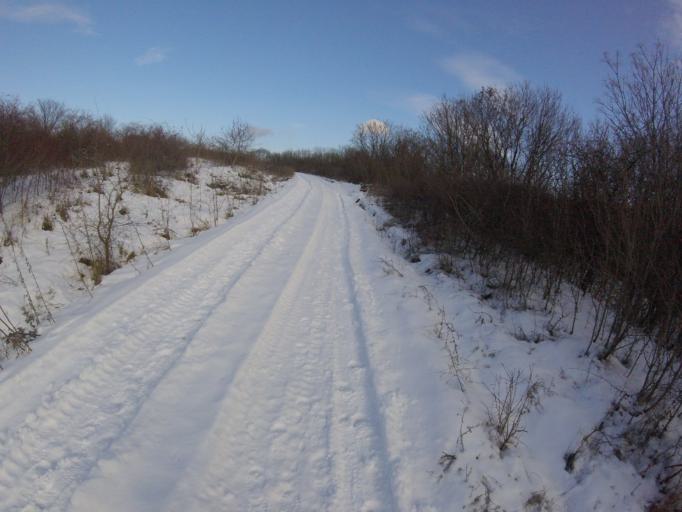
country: HU
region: Pest
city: Szentendre
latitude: 47.6718
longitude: 19.0488
